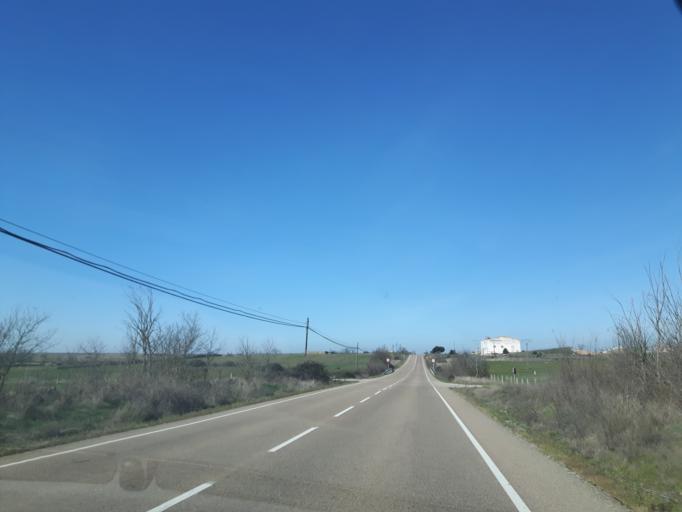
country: ES
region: Castille and Leon
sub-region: Provincia de Salamanca
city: Vitigudino
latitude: 41.0113
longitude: -6.4635
